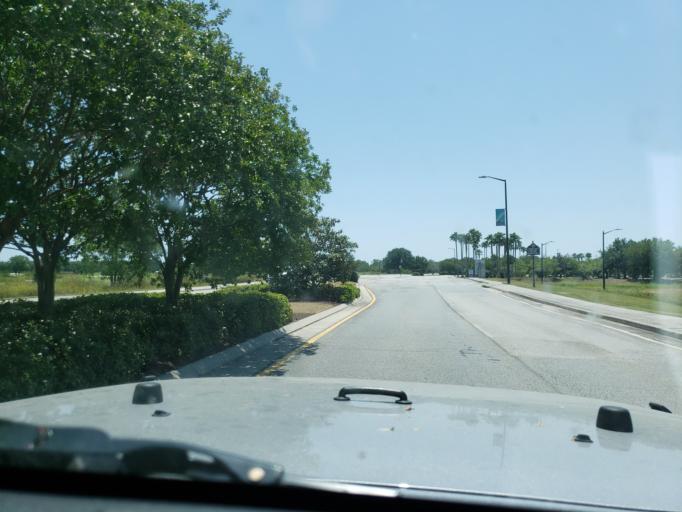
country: US
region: Georgia
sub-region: Chatham County
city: Savannah
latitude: 32.0890
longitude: -81.0873
